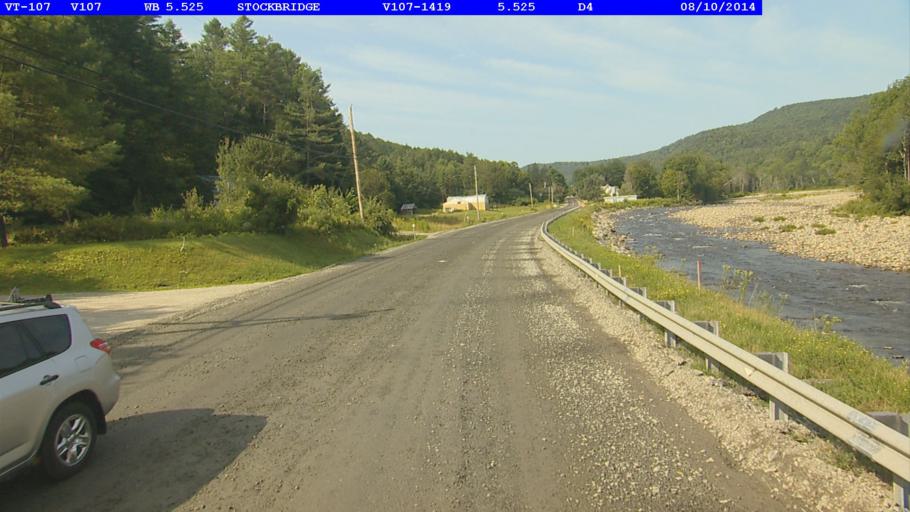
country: US
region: Vermont
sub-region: Orange County
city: Randolph
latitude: 43.7878
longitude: -72.6813
